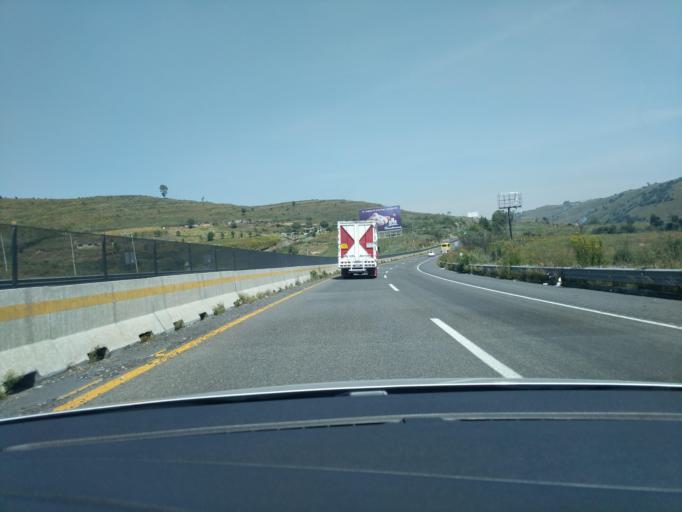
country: MX
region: Mexico
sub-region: Naucalpan de Juarez
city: Rincon Verde
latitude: 19.4984
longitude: -99.3070
